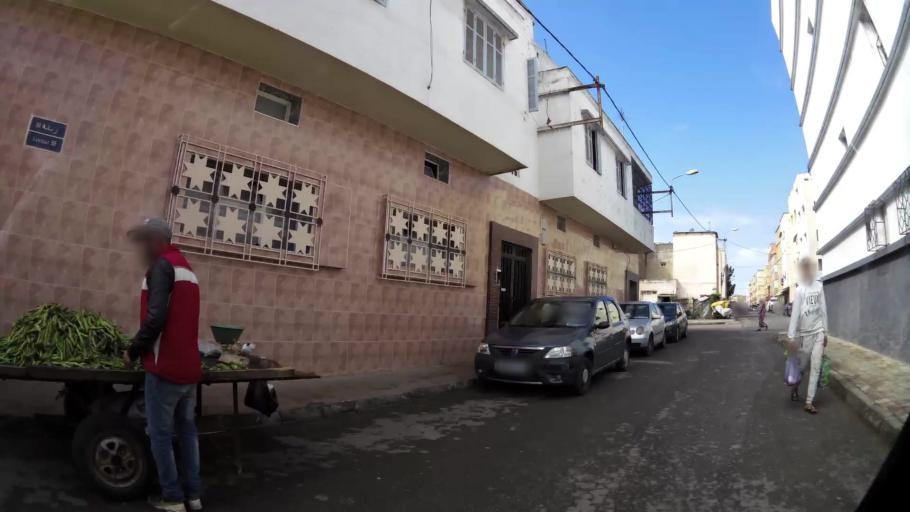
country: MA
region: Grand Casablanca
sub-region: Casablanca
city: Casablanca
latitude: 33.5721
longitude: -7.6726
